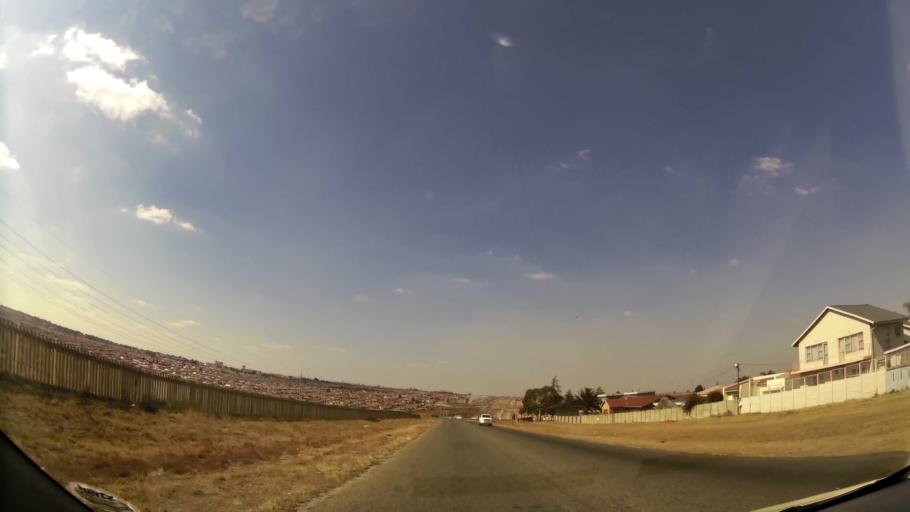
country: ZA
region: Gauteng
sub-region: West Rand District Municipality
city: Randfontein
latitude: -26.1634
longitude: 27.7584
